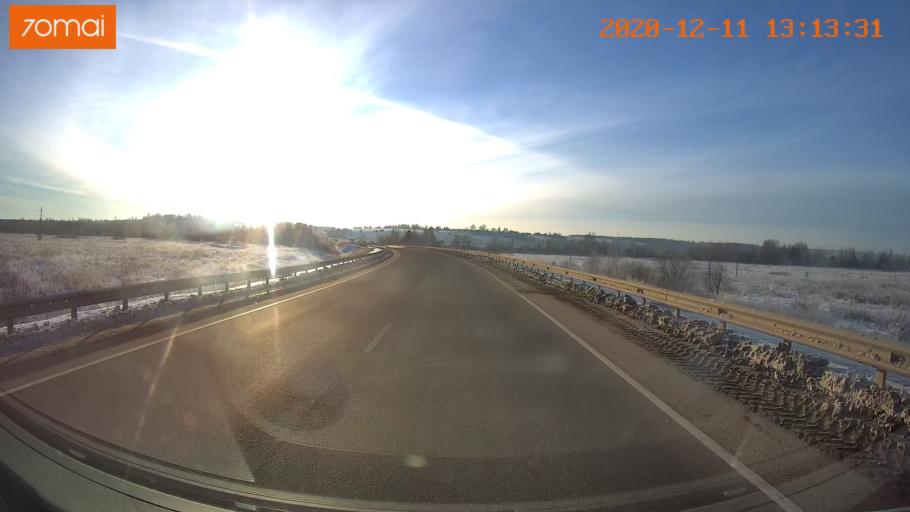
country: RU
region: Kostroma
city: Susanino
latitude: 58.1406
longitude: 41.6080
